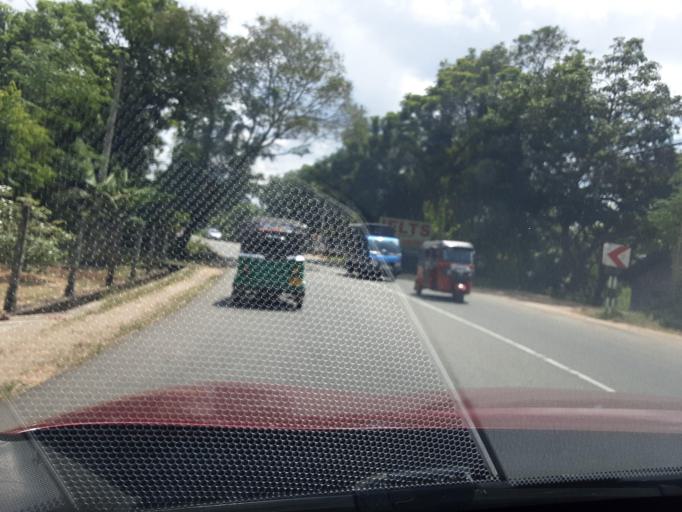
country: LK
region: North Western
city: Kurunegala
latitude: 7.4743
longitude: 80.3318
